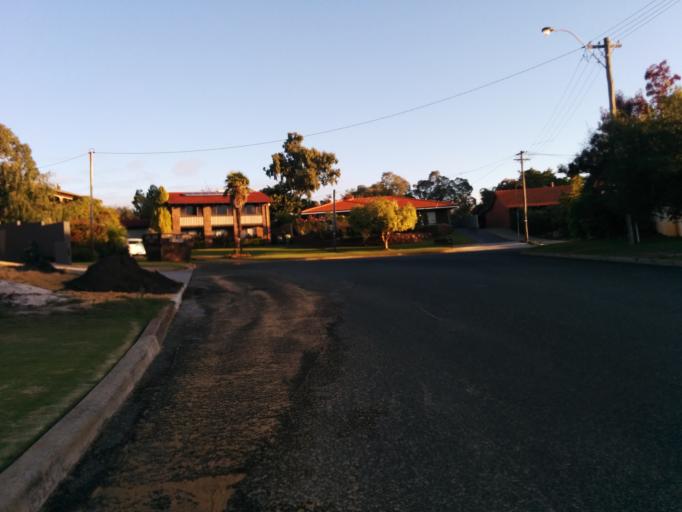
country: AU
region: Western Australia
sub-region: Canning
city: Rossmoyne
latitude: -32.0506
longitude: 115.8608
